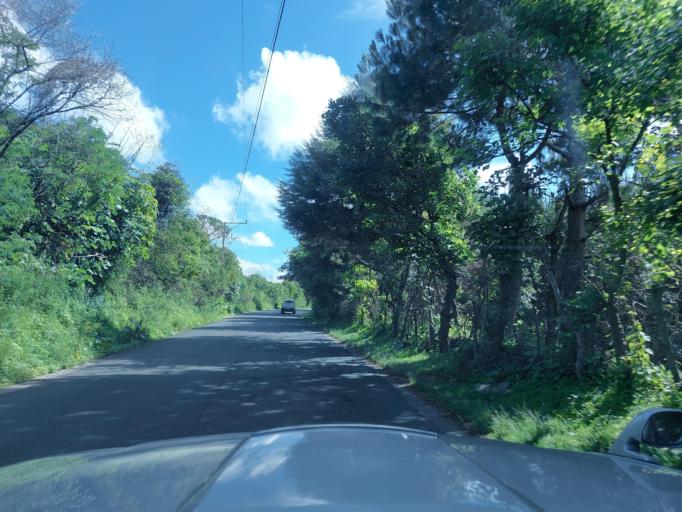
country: GT
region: Chimaltenango
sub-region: Municipio de Zaragoza
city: Zaragoza
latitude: 14.6521
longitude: -90.8975
